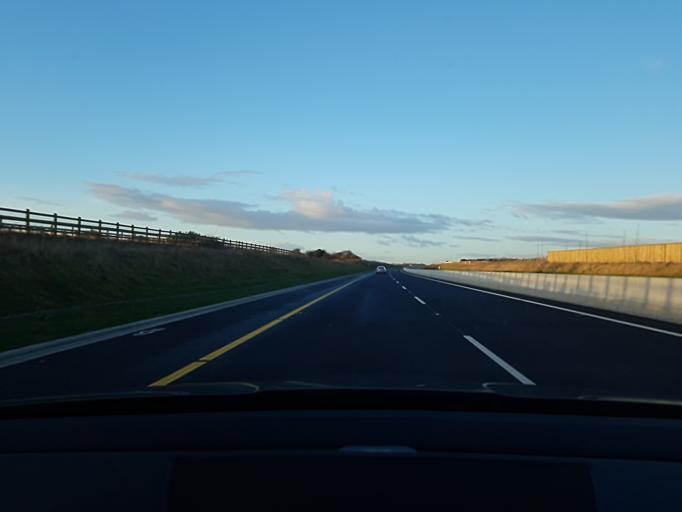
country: IE
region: Connaught
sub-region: County Galway
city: Athenry
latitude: 53.3259
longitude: -8.8032
